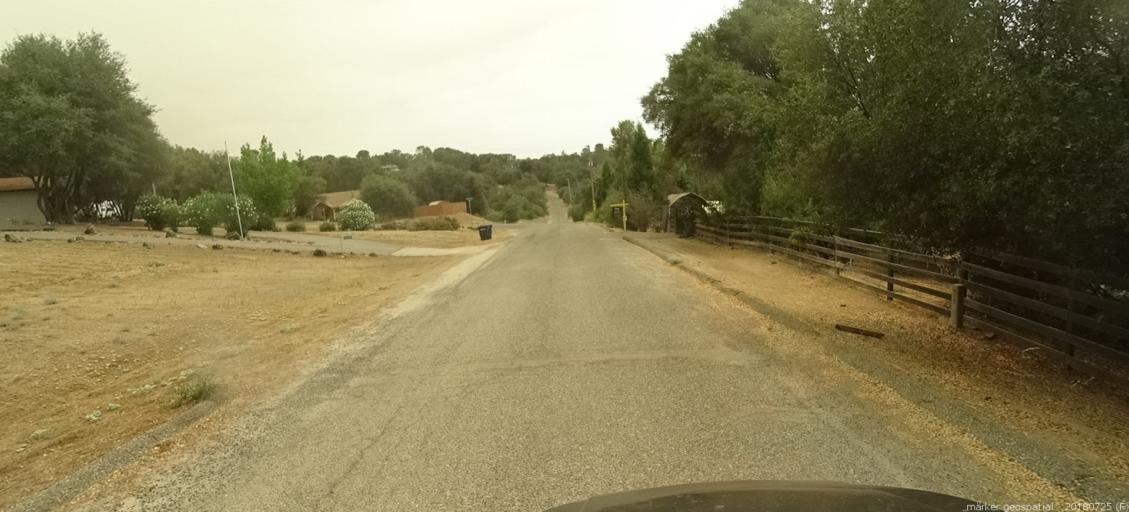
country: US
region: California
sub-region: Madera County
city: Coarsegold
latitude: 37.2196
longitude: -119.6900
